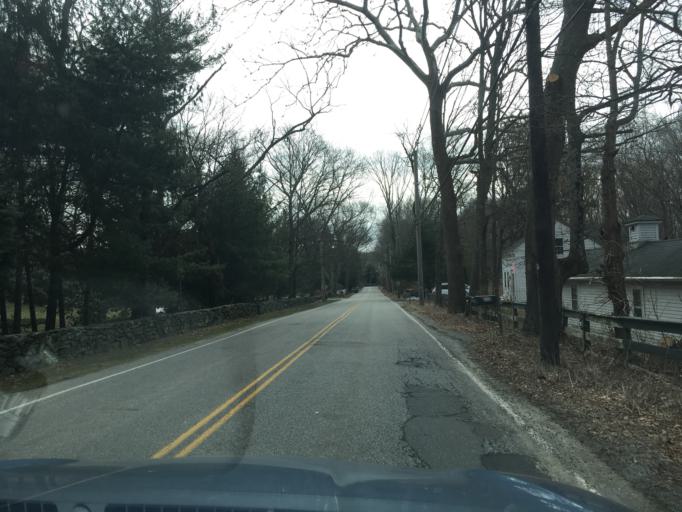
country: US
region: Rhode Island
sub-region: Kent County
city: East Greenwich
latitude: 41.6430
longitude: -71.4490
